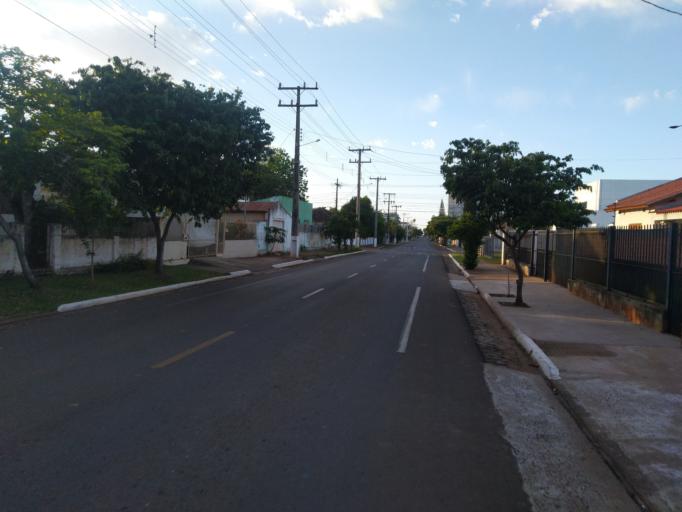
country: BR
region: Rio Grande do Sul
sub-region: Sao Borja
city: Sao Borja
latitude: -28.6524
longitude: -56.0106
